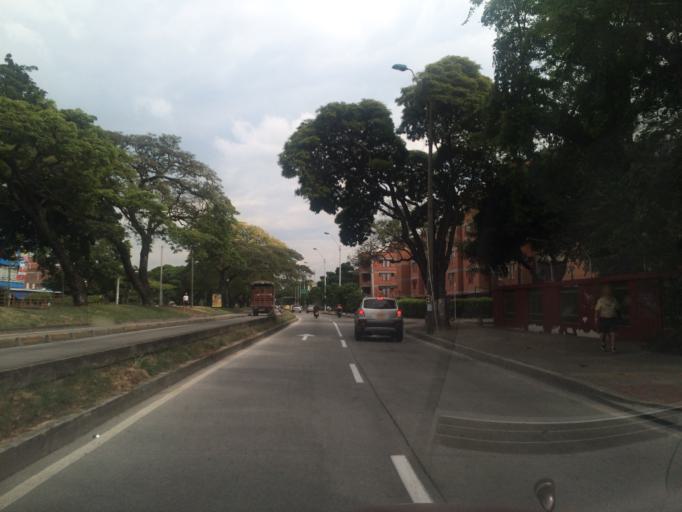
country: CO
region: Valle del Cauca
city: Cali
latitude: 3.4070
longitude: -76.5473
